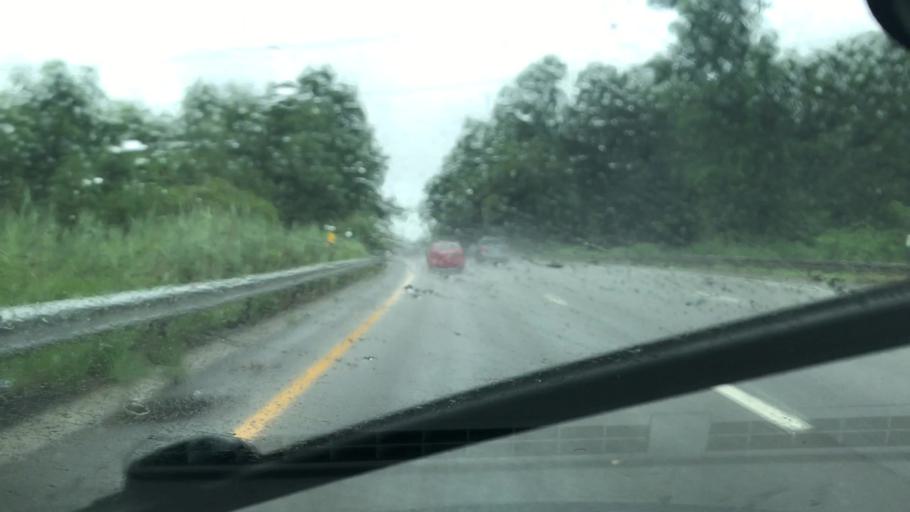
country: US
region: New York
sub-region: Westchester County
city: Briarcliff Manor
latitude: 41.1923
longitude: -73.8060
